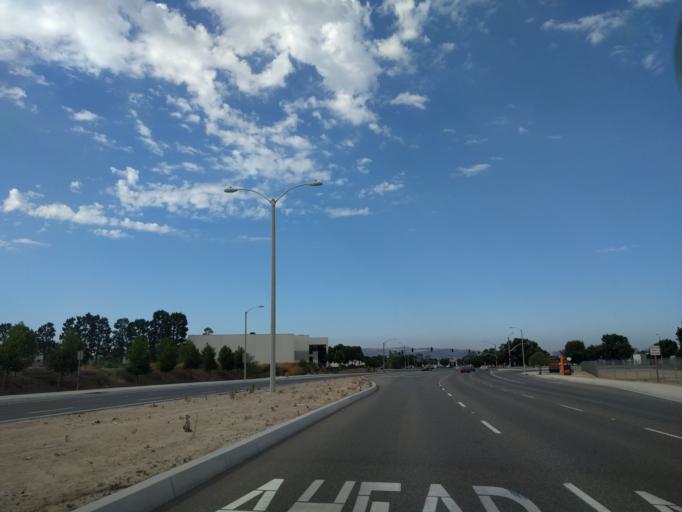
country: US
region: California
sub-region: Orange County
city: Lake Forest
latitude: 33.6645
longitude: -117.7046
